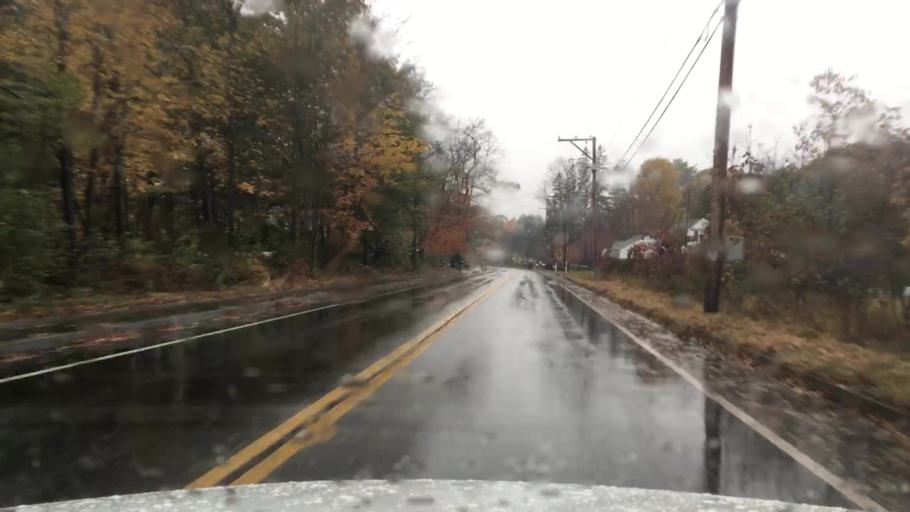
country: US
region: New Hampshire
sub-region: Strafford County
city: Rochester
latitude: 43.3225
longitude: -70.9487
